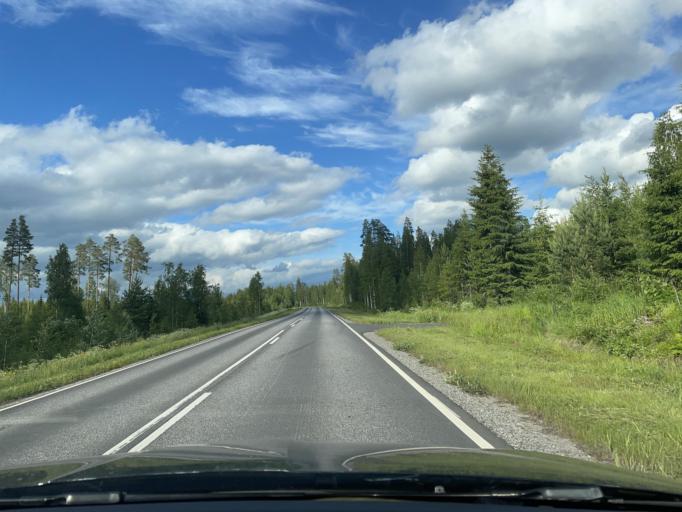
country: FI
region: Central Finland
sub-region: Jyvaeskylae
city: Petaejaevesi
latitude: 62.0917
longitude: 25.1536
